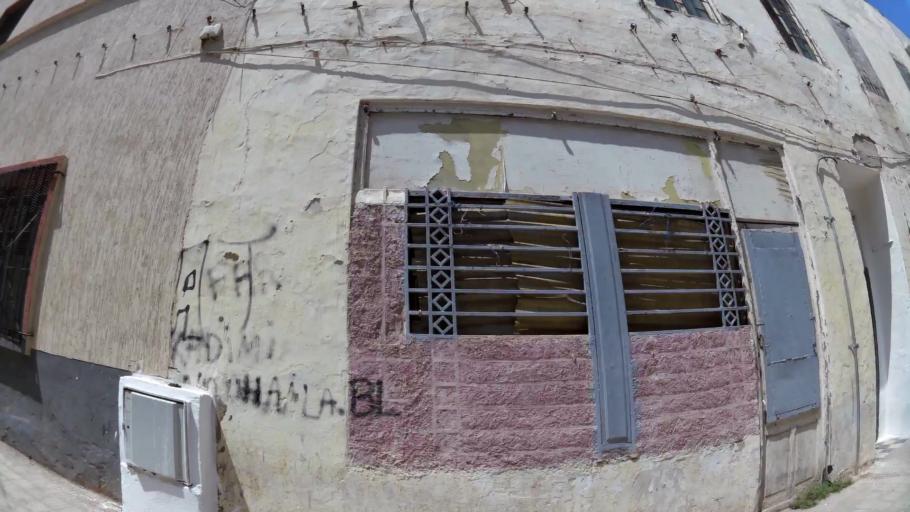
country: MA
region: Rabat-Sale-Zemmour-Zaer
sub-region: Rabat
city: Rabat
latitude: 34.0261
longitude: -6.8453
